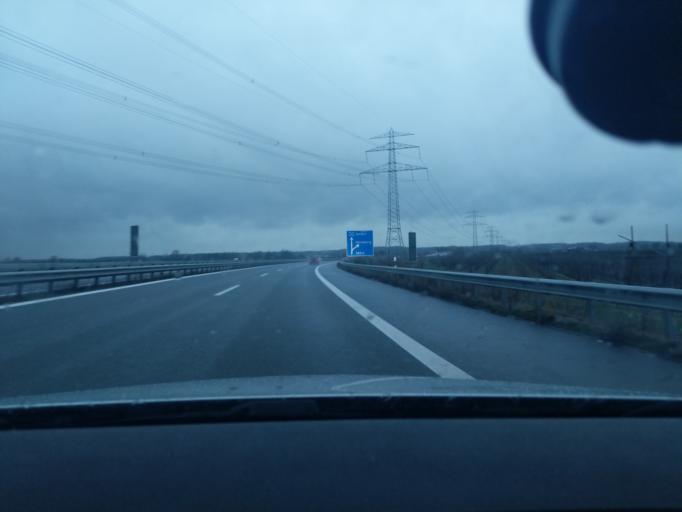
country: DE
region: Lower Saxony
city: Neuenkirchen
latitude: 53.5117
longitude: 9.6115
